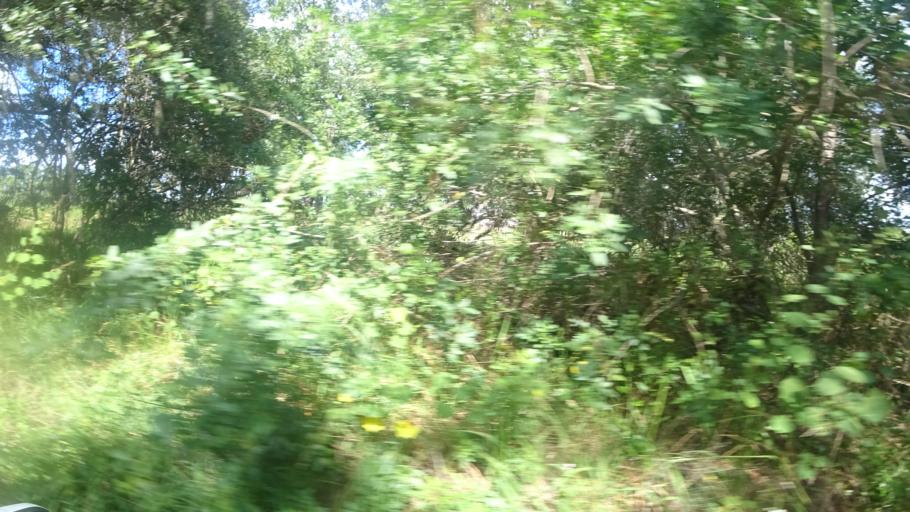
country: US
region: Florida
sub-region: Hillsborough County
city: Sun City Center
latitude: 27.6434
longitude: -82.3609
